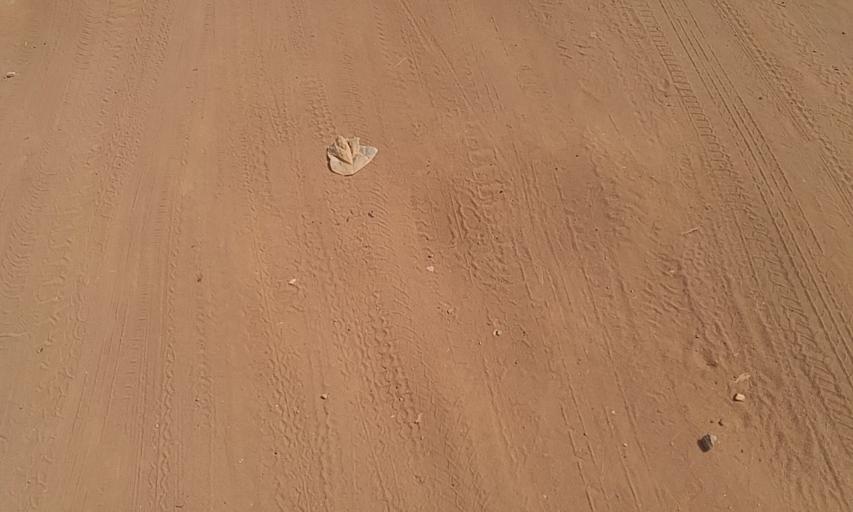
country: TG
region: Maritime
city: Lome
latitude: 6.1723
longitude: 1.1847
